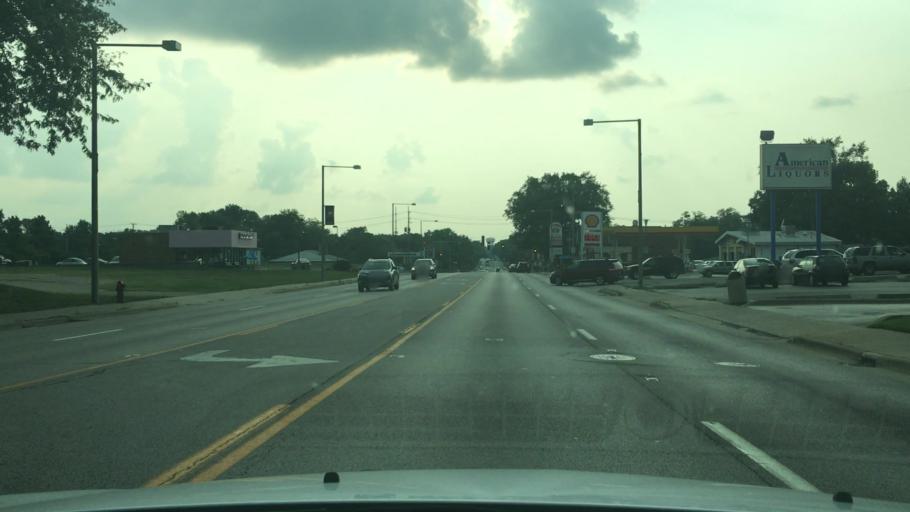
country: US
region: Illinois
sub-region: DeKalb County
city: DeKalb
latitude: 41.9309
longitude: -88.7557
